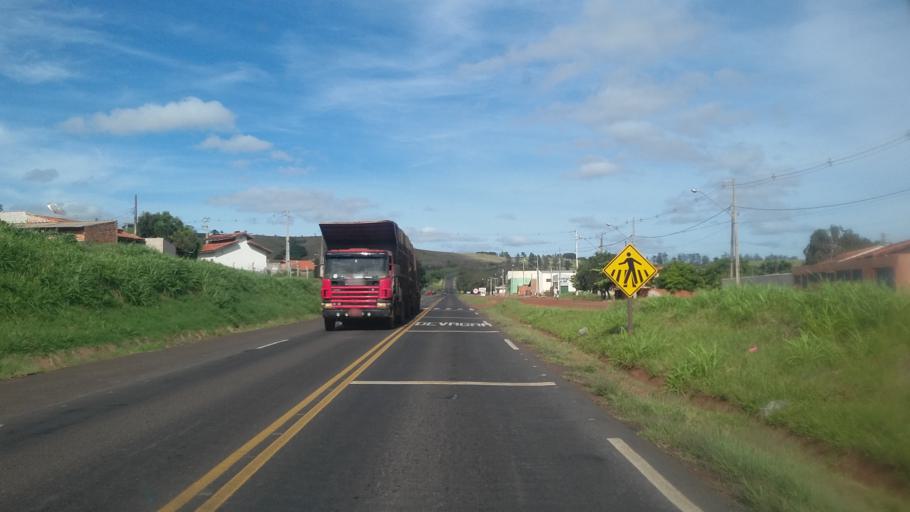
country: BR
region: Parana
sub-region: Santo Antonio Da Platina
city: Santo Antonio da Platina
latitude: -23.2763
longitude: -50.0667
